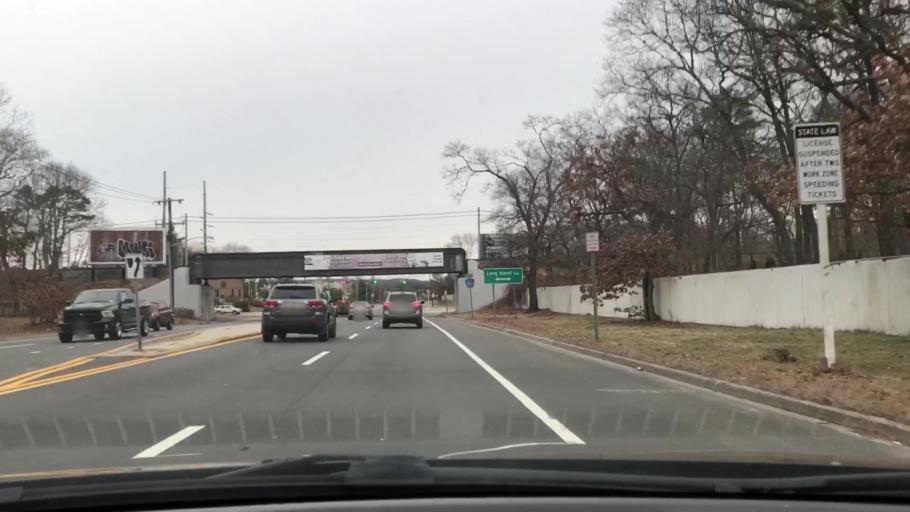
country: US
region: New York
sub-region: Suffolk County
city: Farmingville
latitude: 40.8148
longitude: -73.0200
